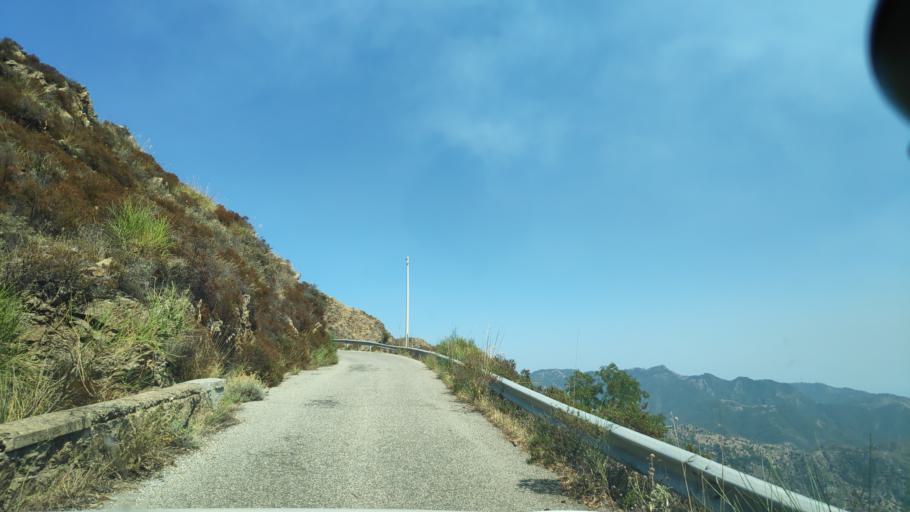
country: IT
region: Calabria
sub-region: Provincia di Reggio Calabria
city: Bova
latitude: 38.0026
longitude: 15.9294
